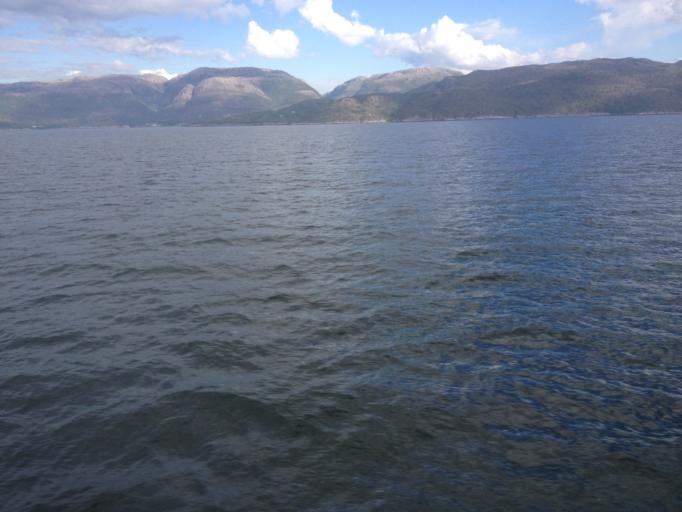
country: NO
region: Sor-Trondelag
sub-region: Snillfjord
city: Krokstadora
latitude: 63.5448
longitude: 9.2567
